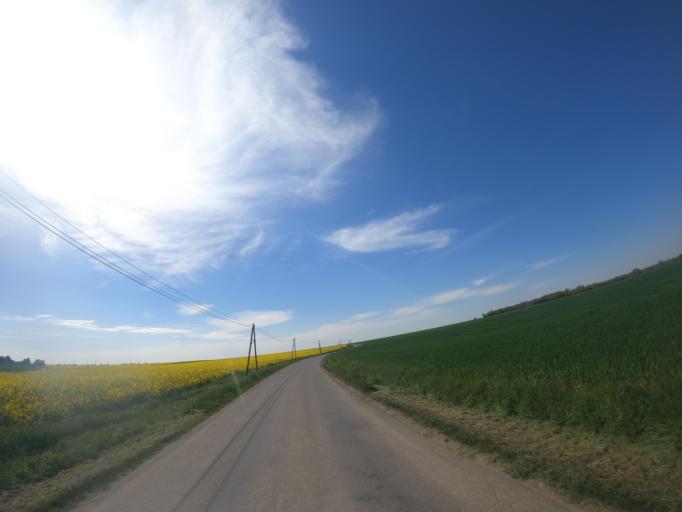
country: FR
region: Poitou-Charentes
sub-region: Departement des Deux-Sevres
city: Airvault
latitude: 46.8867
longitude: -0.1506
